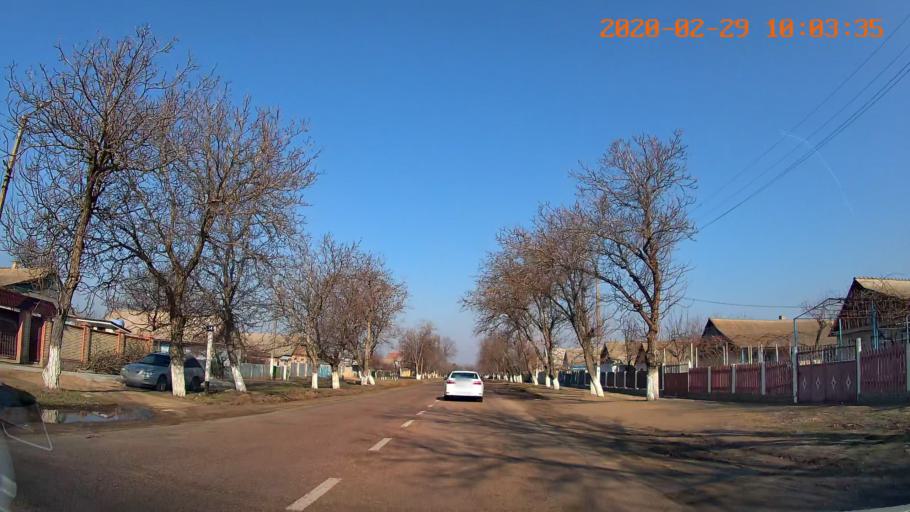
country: MD
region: Causeni
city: Chitcani
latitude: 46.7916
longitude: 29.6797
